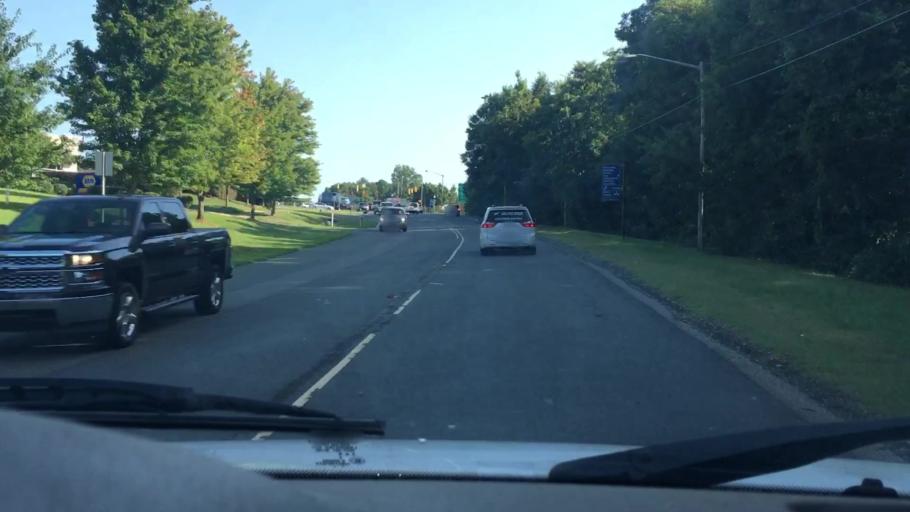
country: US
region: North Carolina
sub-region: Mecklenburg County
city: Cornelius
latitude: 35.4817
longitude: -80.8727
